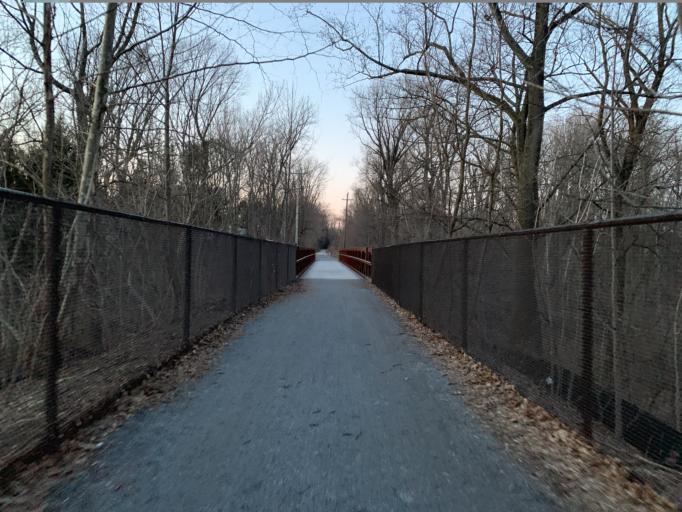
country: US
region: Pennsylvania
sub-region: Montgomery County
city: Rockledge
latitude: 40.0860
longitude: -75.0823
